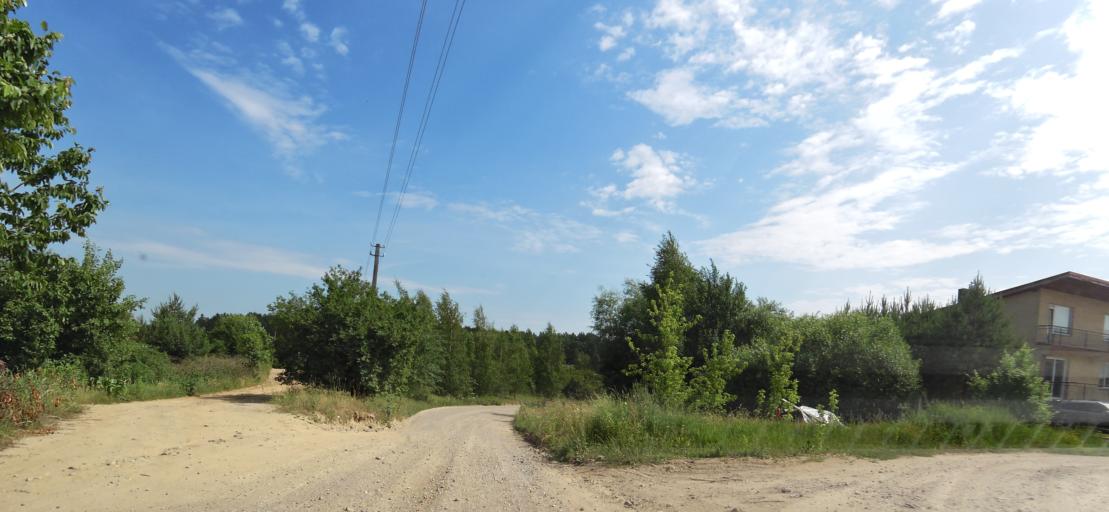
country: LT
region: Vilnius County
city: Pasilaiciai
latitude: 54.7485
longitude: 25.2277
